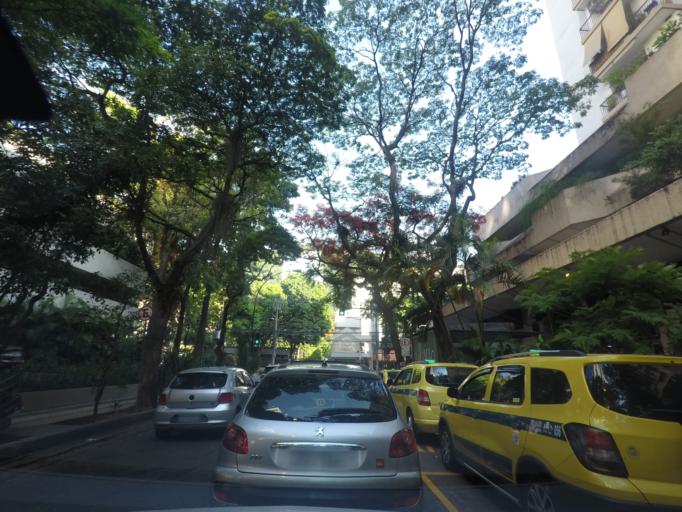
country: BR
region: Rio de Janeiro
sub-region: Rio De Janeiro
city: Rio de Janeiro
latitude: -22.9768
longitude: -43.2290
